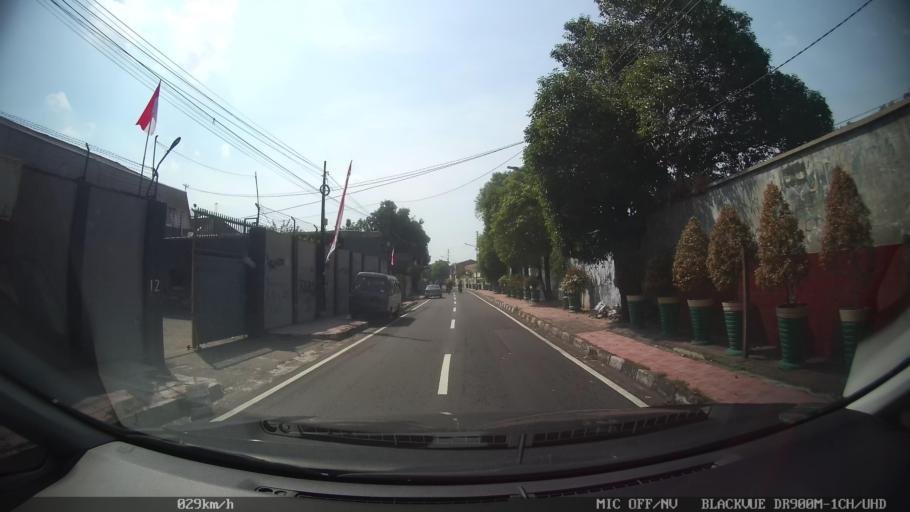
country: ID
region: Daerah Istimewa Yogyakarta
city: Yogyakarta
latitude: -7.7879
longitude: 110.3605
